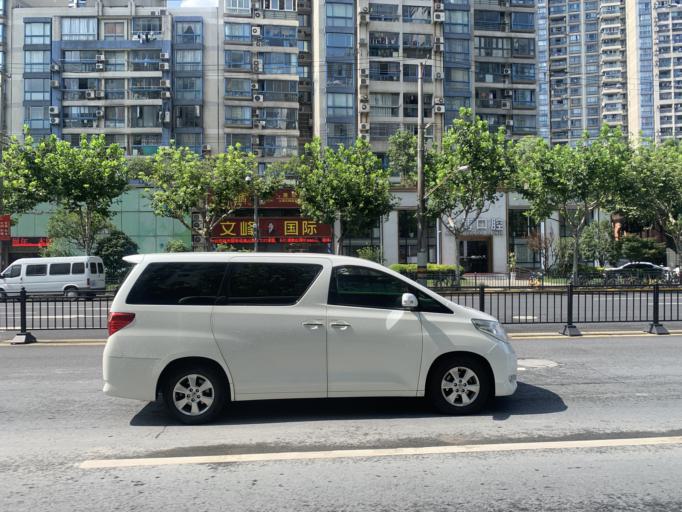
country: CN
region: Shanghai Shi
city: Luwan
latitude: 31.2147
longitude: 121.4903
